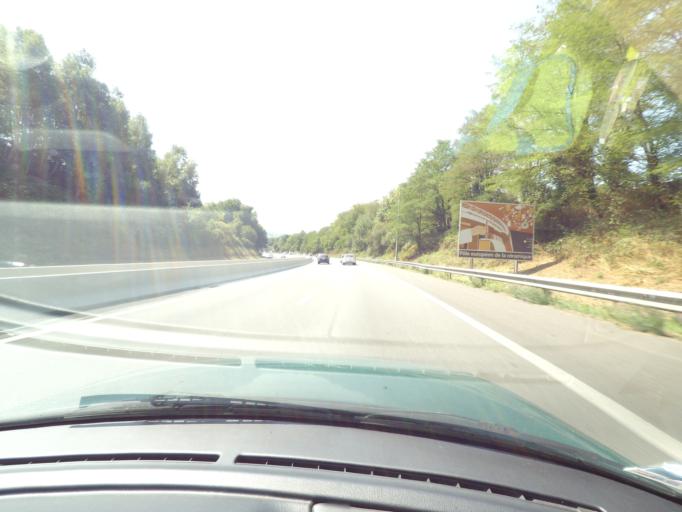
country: FR
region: Limousin
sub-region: Departement de la Haute-Vienne
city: Limoges
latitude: 45.8539
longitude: 1.2766
